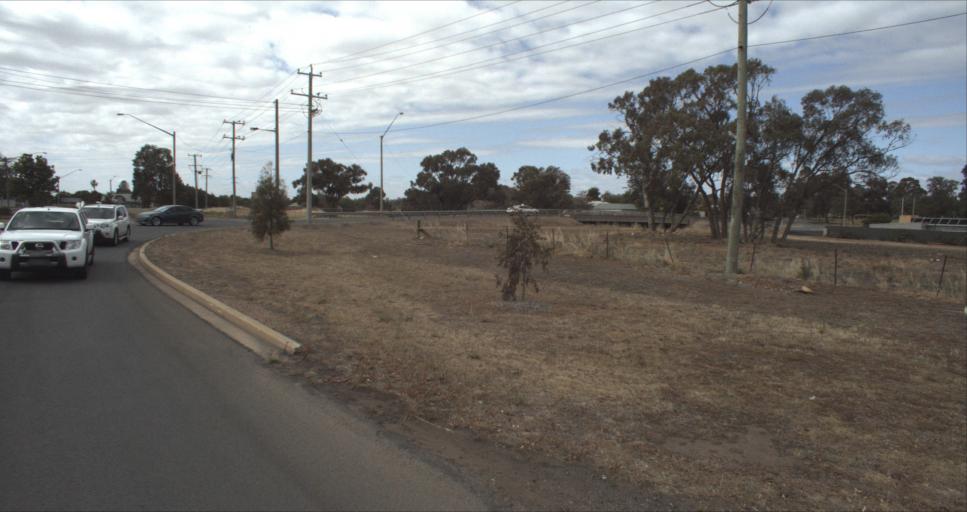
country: AU
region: New South Wales
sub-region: Leeton
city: Leeton
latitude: -34.5555
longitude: 146.4008
